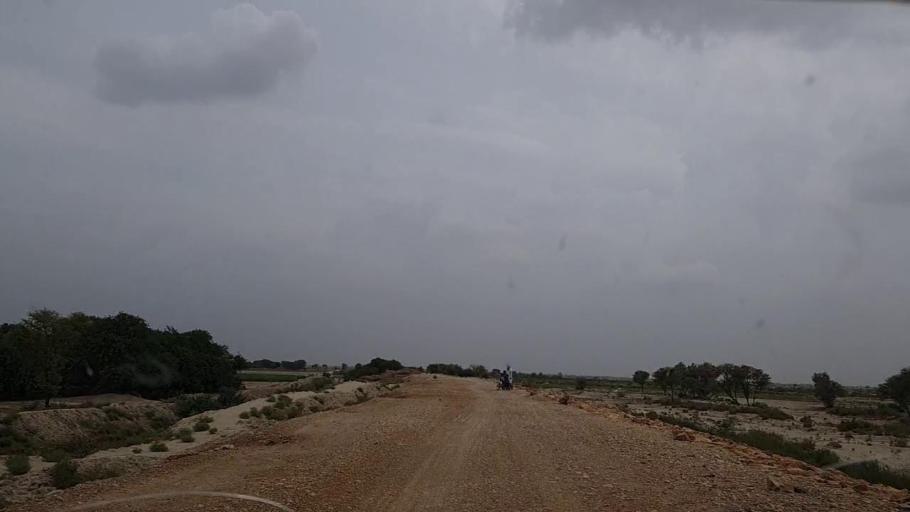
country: PK
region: Sindh
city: Johi
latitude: 26.7217
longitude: 67.5789
